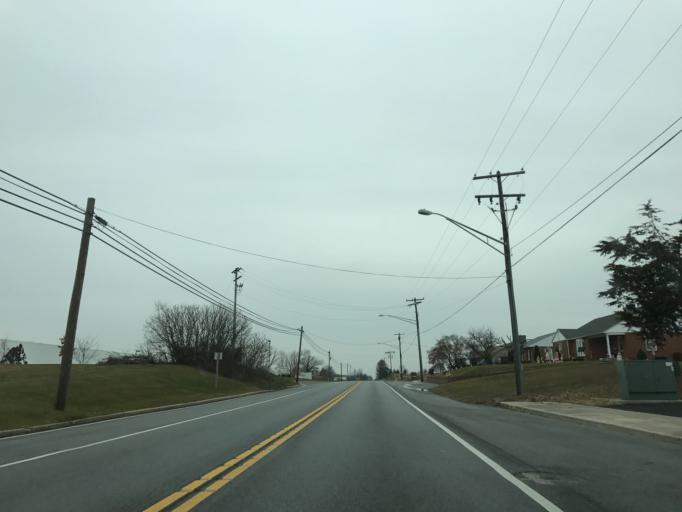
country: US
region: Maryland
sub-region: Carroll County
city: Taneytown
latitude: 39.6648
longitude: -77.1850
